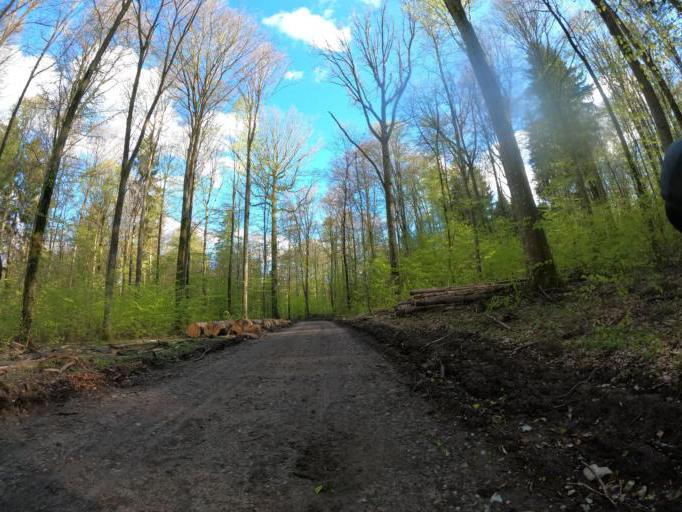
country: DE
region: Baden-Wuerttemberg
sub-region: Karlsruhe Region
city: Gechingen
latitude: 48.6891
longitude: 8.8516
